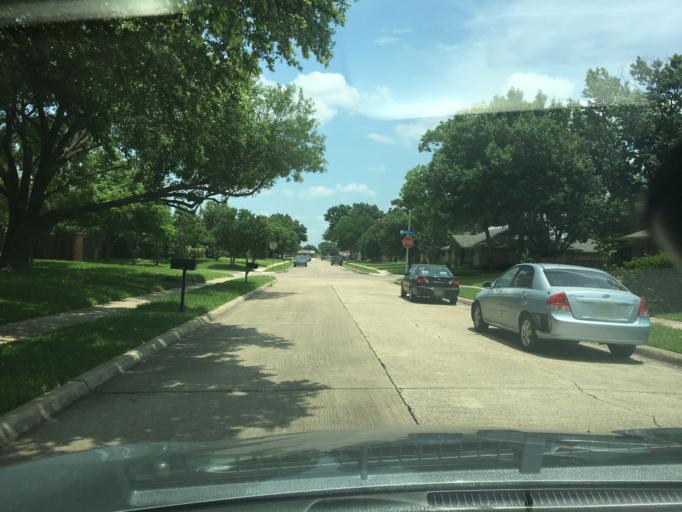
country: US
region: Texas
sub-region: Dallas County
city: Richardson
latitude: 32.9539
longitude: -96.6857
